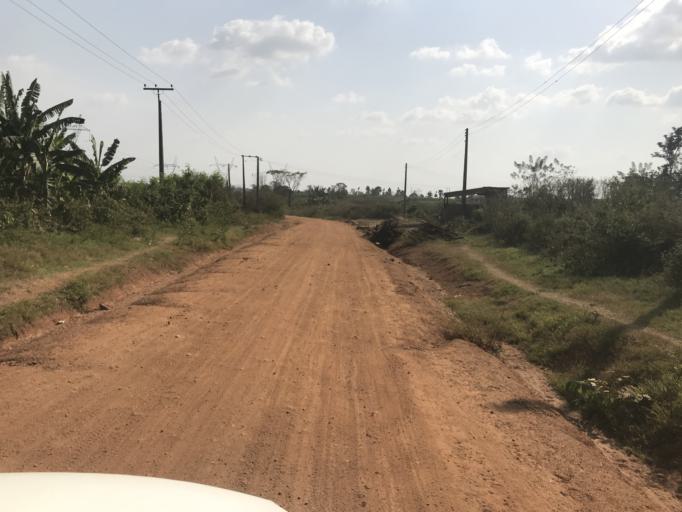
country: NG
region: Osun
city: Osogbo
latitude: 7.8359
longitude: 4.5712
